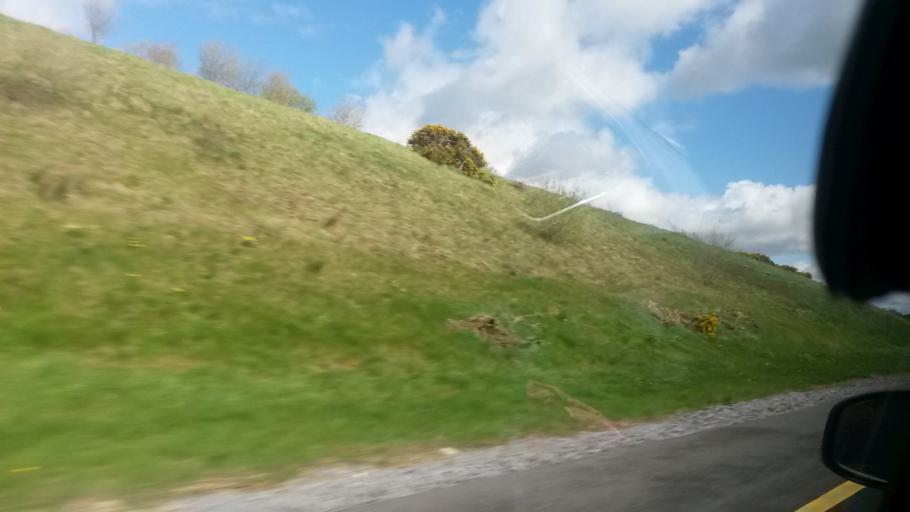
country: IE
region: Munster
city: Cahir
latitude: 52.3924
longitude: -7.9246
